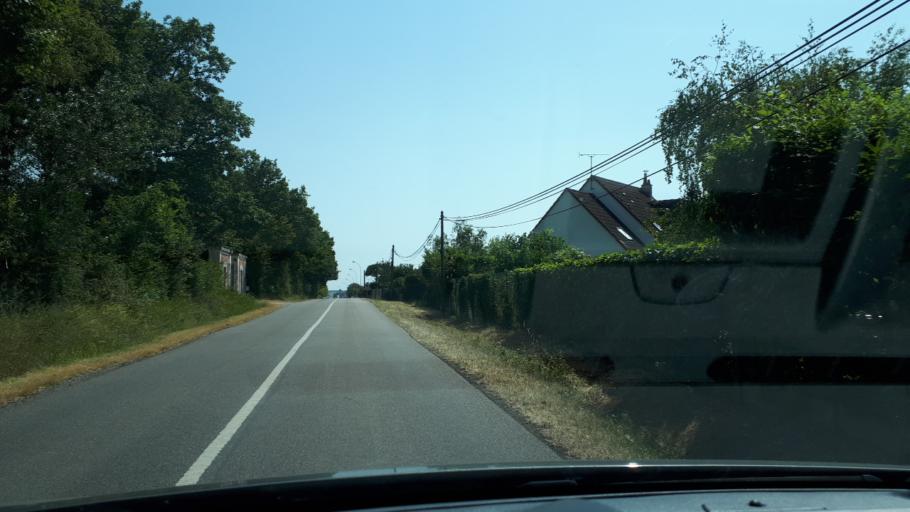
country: FR
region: Centre
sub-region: Departement du Loir-et-Cher
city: Saint-Ouen
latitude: 47.8188
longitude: 1.0688
